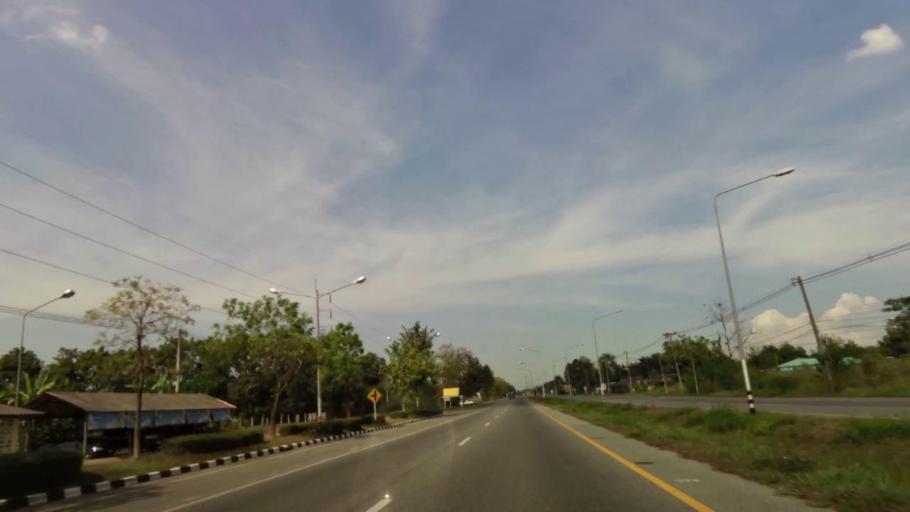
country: TH
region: Uttaradit
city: Tron
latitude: 17.5211
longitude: 100.2176
